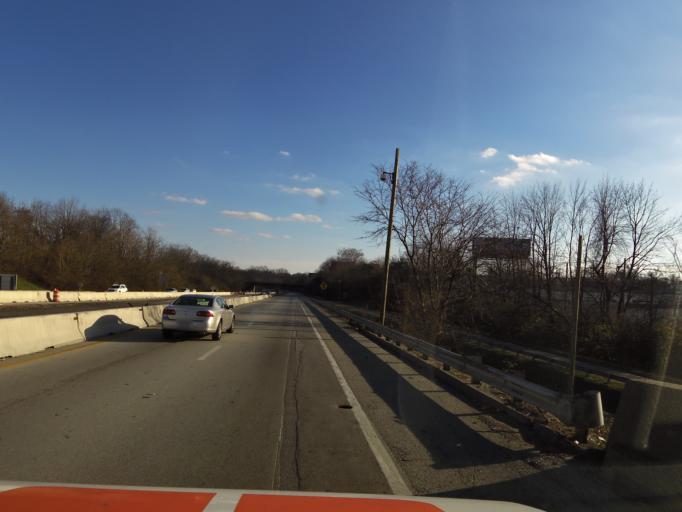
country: US
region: Indiana
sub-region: Clark County
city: Jeffersonville
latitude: 38.2563
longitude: -85.7216
